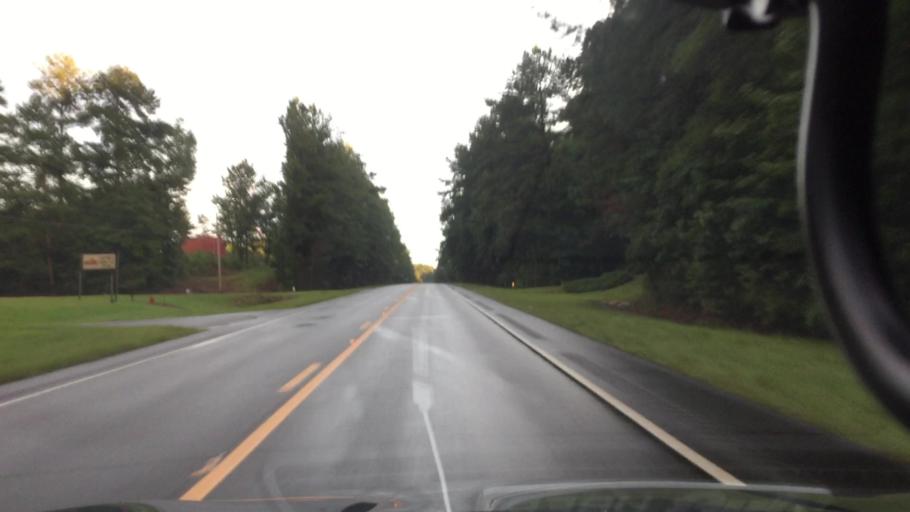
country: US
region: Alabama
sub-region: Coffee County
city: New Brockton
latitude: 31.5613
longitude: -85.9240
